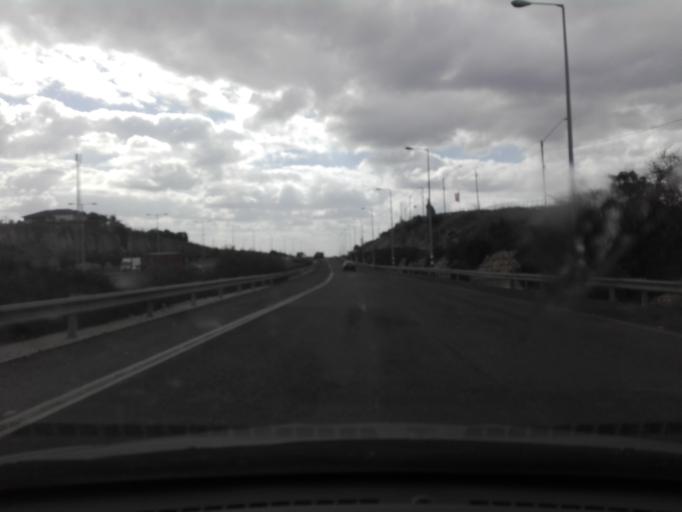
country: IL
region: Haifa
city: Daliyat el Karmil
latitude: 32.6350
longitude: 35.0640
